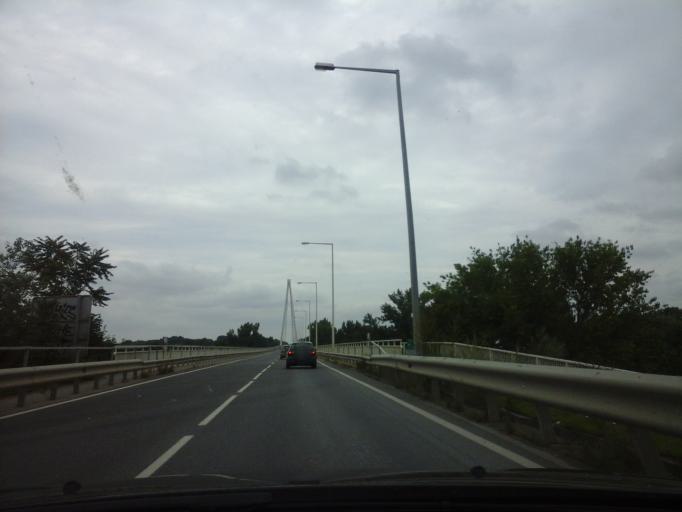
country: AT
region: Lower Austria
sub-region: Politischer Bezirk Bruck an der Leitha
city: Bad Deutsch-Altenburg
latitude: 48.1410
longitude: 16.9118
